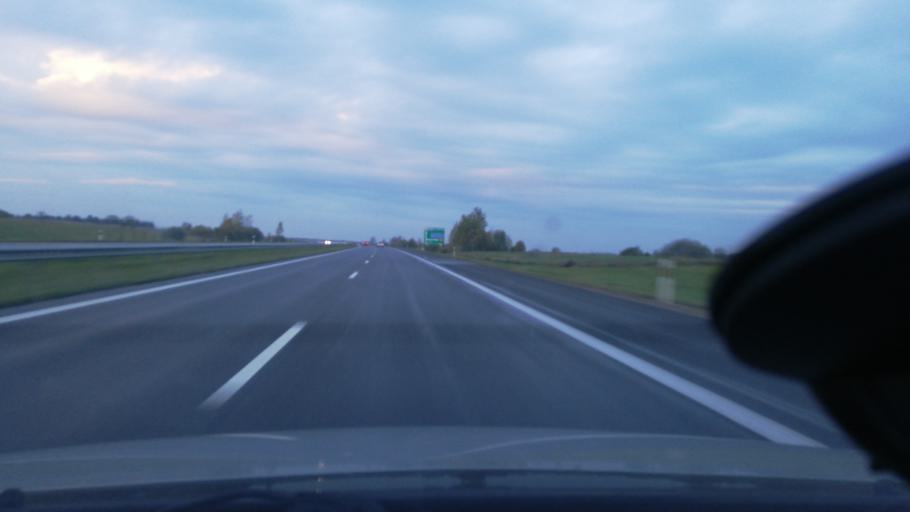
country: LT
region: Klaipedos apskritis
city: Gargzdai
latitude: 55.7316
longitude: 21.3973
